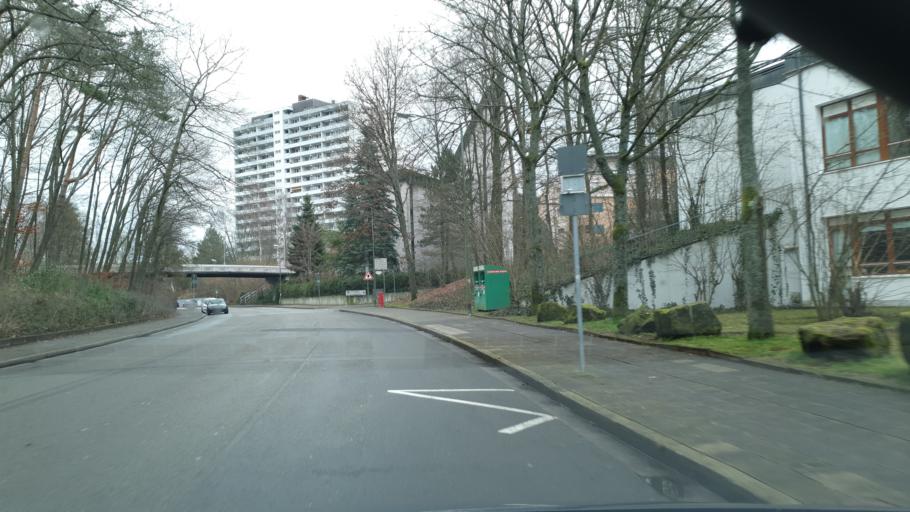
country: DE
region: Rheinland-Pfalz
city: Kaiserslautern
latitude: 49.4293
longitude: 7.7794
